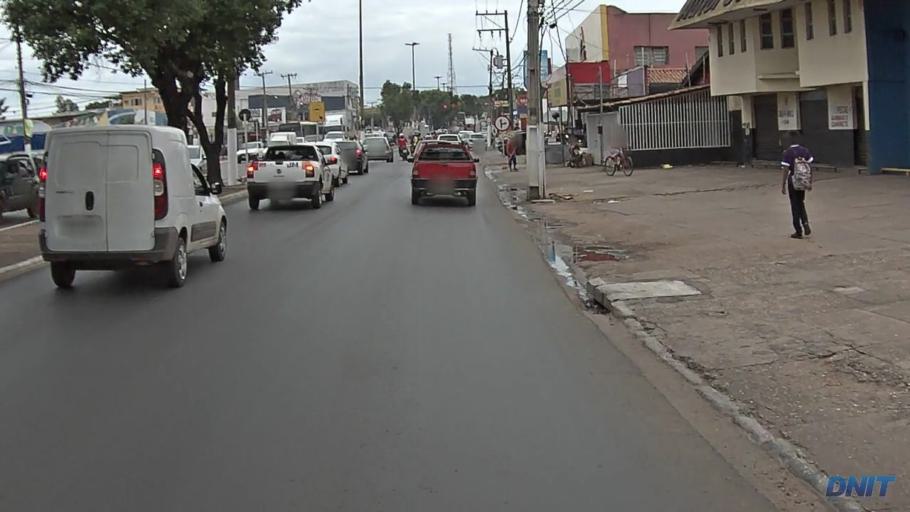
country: BR
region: Mato Grosso
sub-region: Varzea Grande
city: Varzea Grande
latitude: -15.6469
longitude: -56.1525
